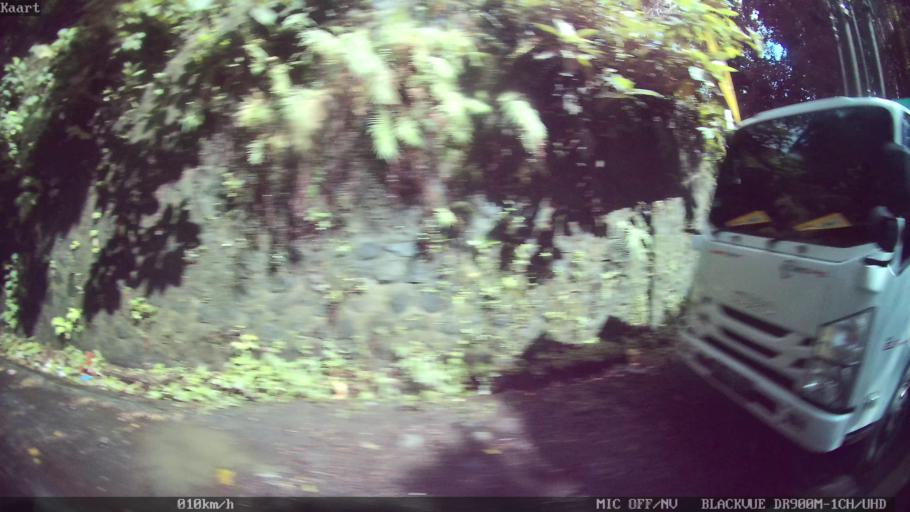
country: ID
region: Bali
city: Banjar Tebongkang
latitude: -8.5466
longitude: 115.2544
